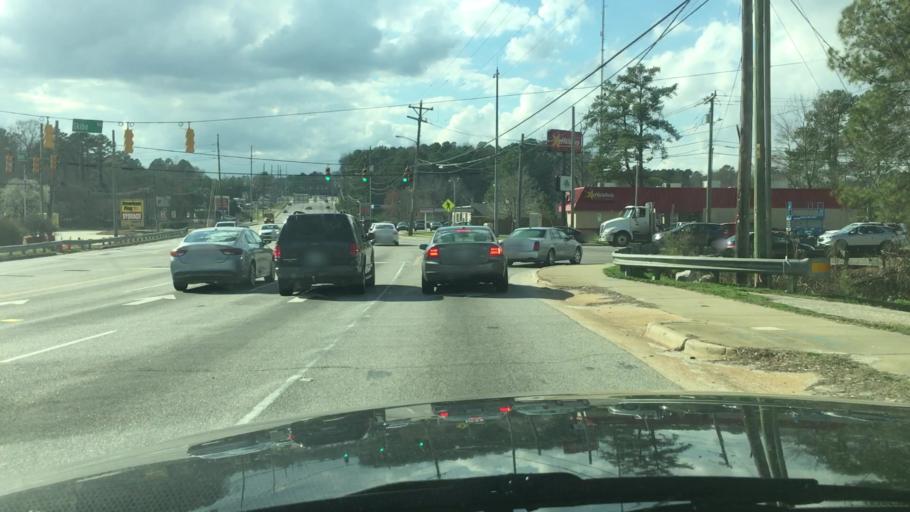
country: US
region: North Carolina
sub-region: Cumberland County
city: Hope Mills
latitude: 35.0445
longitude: -78.9756
